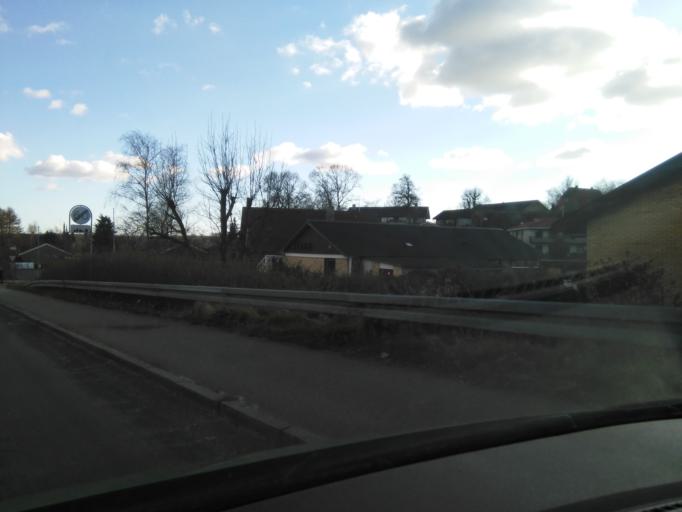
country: DK
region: Central Jutland
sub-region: Silkeborg Kommune
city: Silkeborg
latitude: 56.1798
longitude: 9.5189
